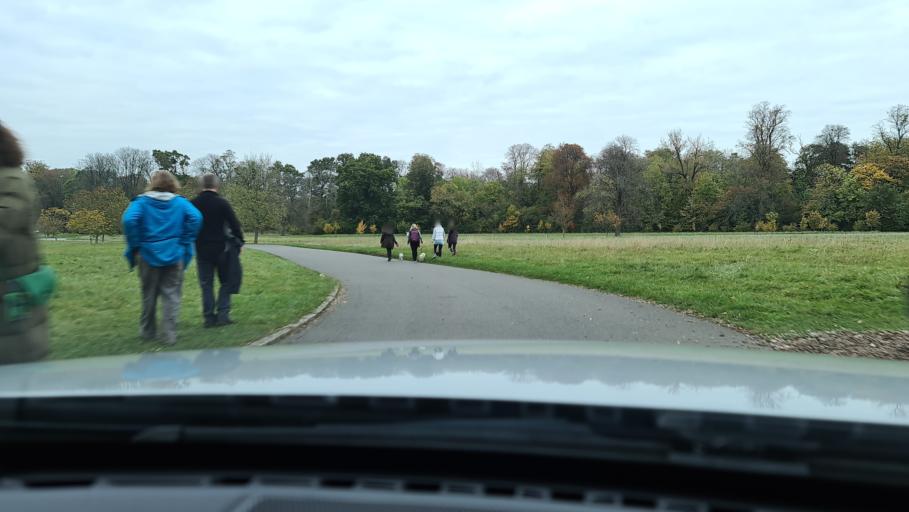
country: GB
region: England
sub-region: Buckinghamshire
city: Waddesdon
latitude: 51.8404
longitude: -0.9239
